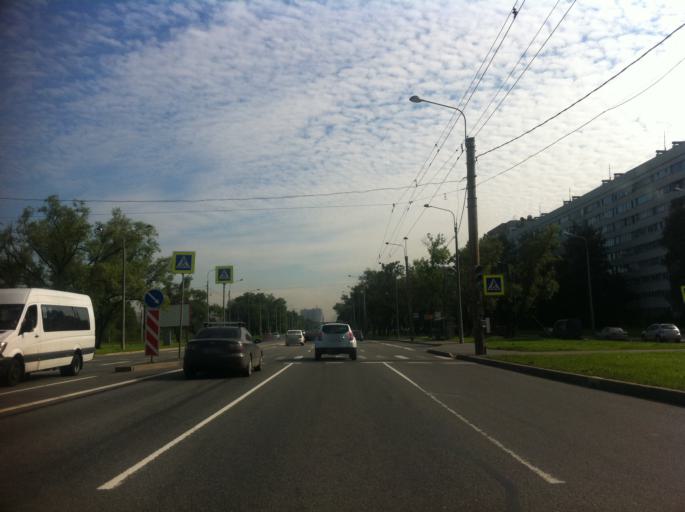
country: RU
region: St.-Petersburg
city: Uritsk
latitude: 59.8363
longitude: 30.1992
